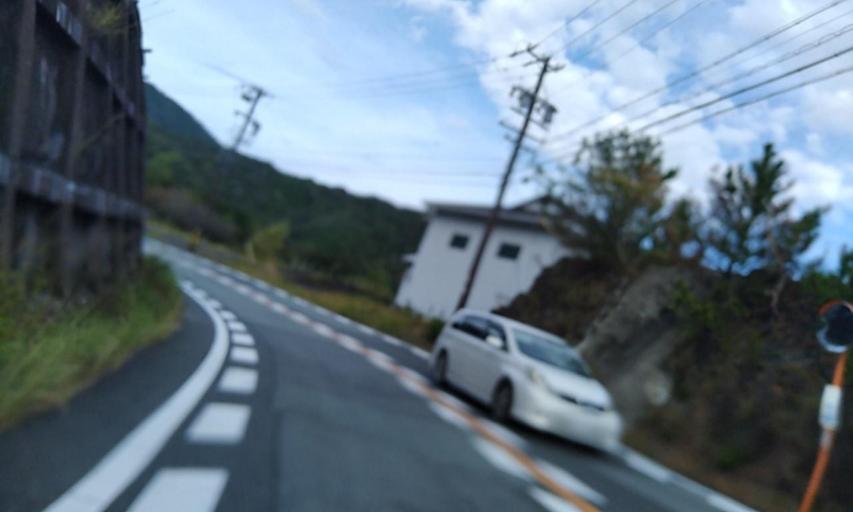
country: JP
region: Mie
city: Ise
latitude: 34.3204
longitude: 136.6506
